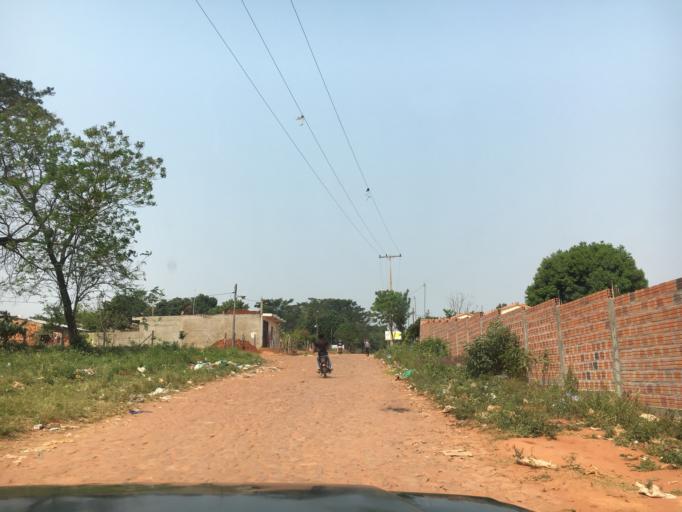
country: PY
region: Central
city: Villa Elisa
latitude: -25.3843
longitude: -57.5698
